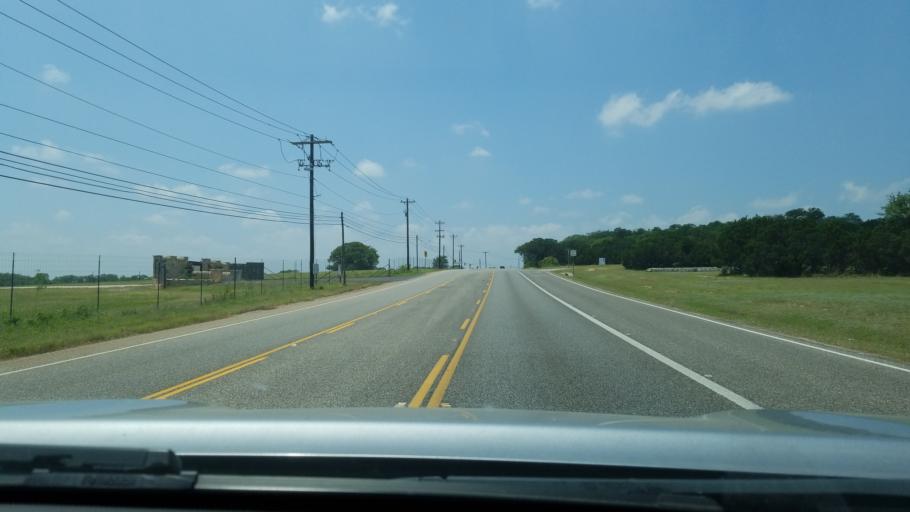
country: US
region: Texas
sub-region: Hays County
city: Woodcreek
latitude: 30.0180
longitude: -98.1442
